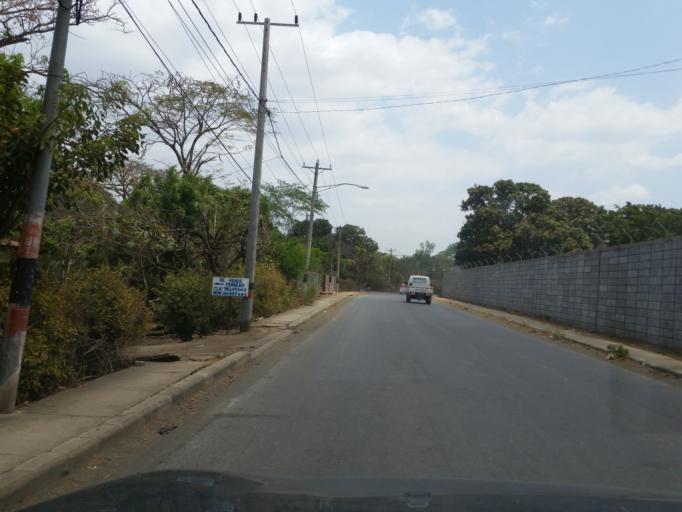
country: NI
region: Managua
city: Managua
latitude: 12.1242
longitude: -86.1693
